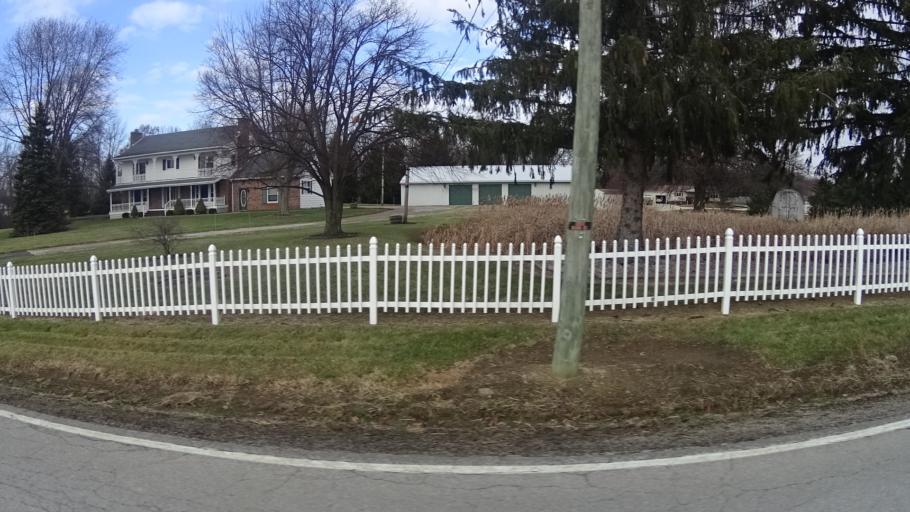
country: US
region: Ohio
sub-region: Lorain County
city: Camden
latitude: 41.2761
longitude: -82.3248
